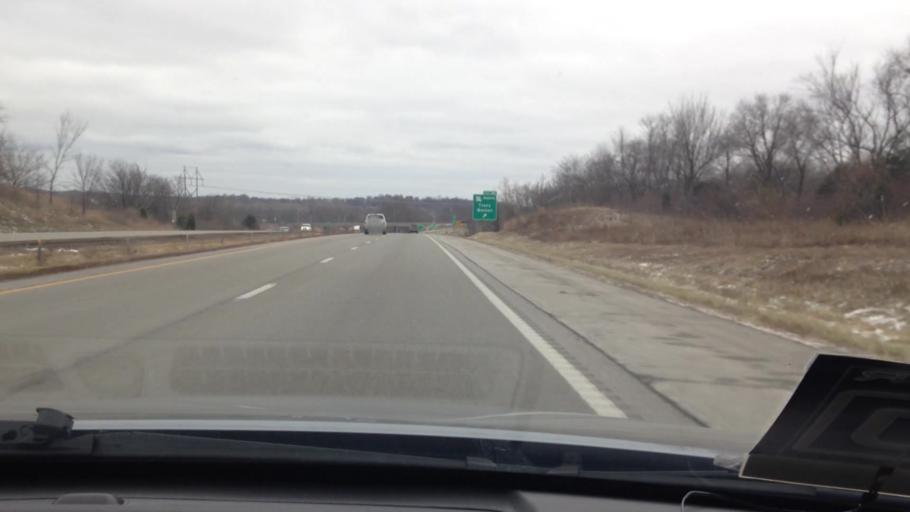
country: US
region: Missouri
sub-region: Platte County
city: Platte City
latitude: 39.3897
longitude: -94.7896
